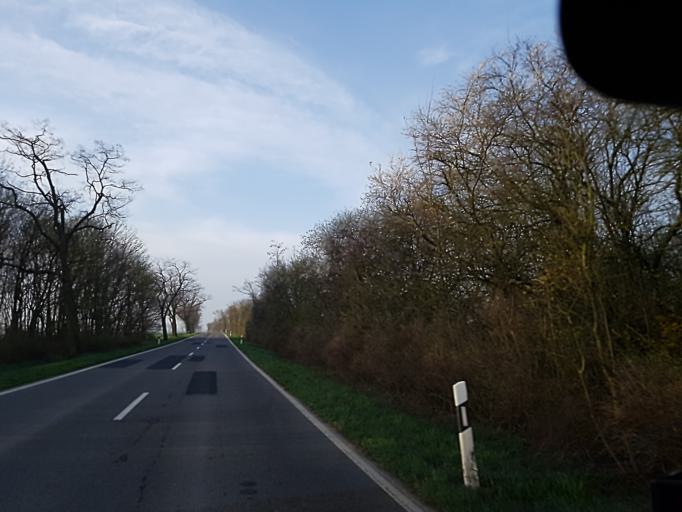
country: DE
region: Brandenburg
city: Muhlberg
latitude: 51.4424
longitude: 13.2691
